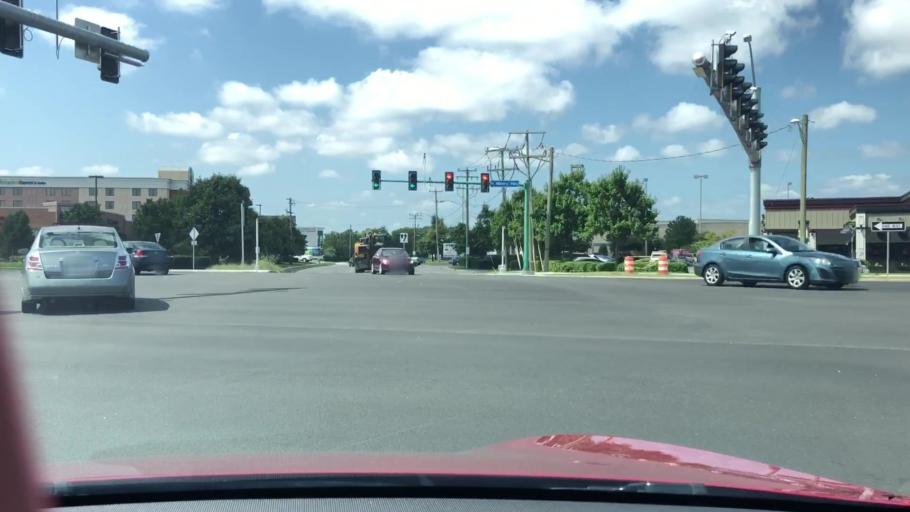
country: US
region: Virginia
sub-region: City of Norfolk
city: Norfolk
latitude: 36.8632
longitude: -76.2102
